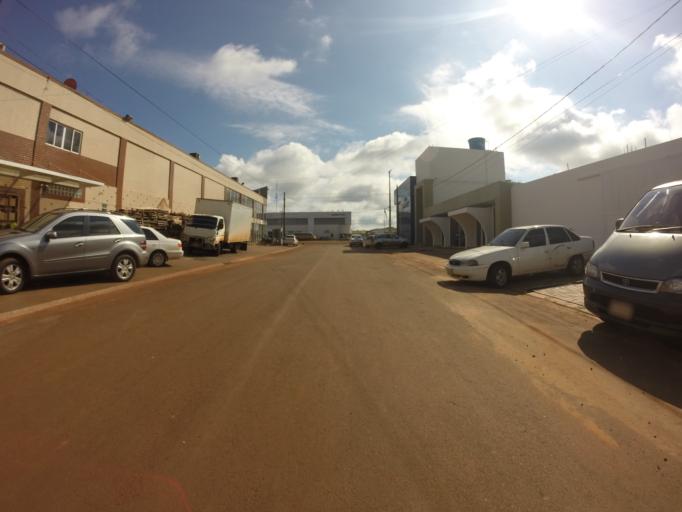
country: PY
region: Alto Parana
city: Ciudad del Este
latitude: -25.3914
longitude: -54.6392
